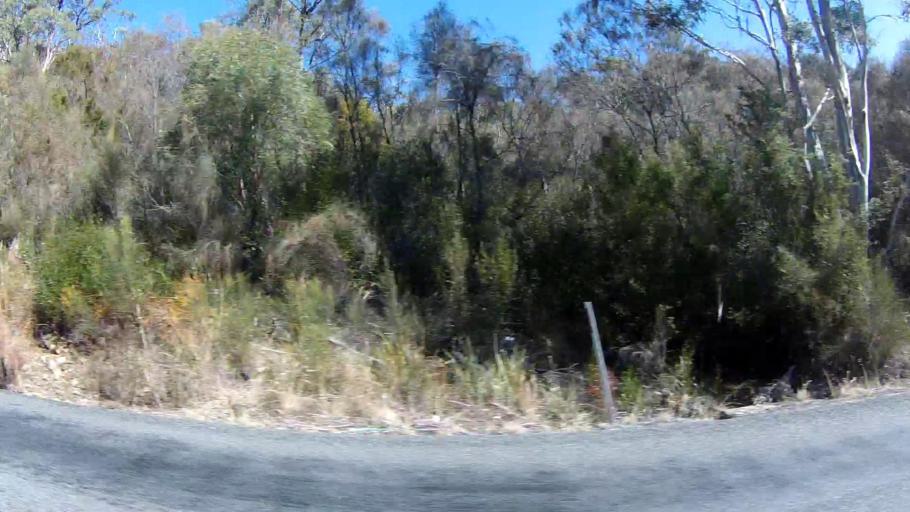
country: AU
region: Tasmania
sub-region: Sorell
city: Sorell
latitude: -42.5574
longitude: 147.8331
